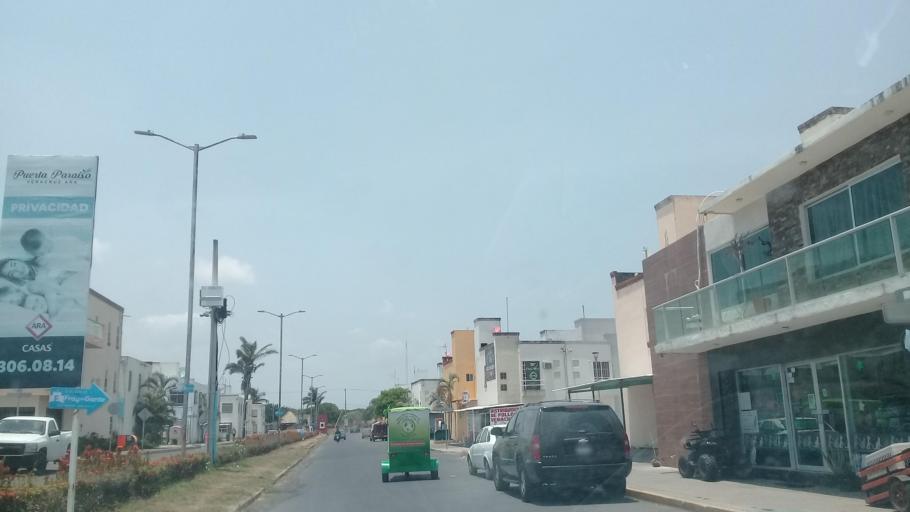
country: MX
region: Veracruz
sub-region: Veracruz
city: Hacienda Sotavento
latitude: 19.1304
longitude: -96.1754
